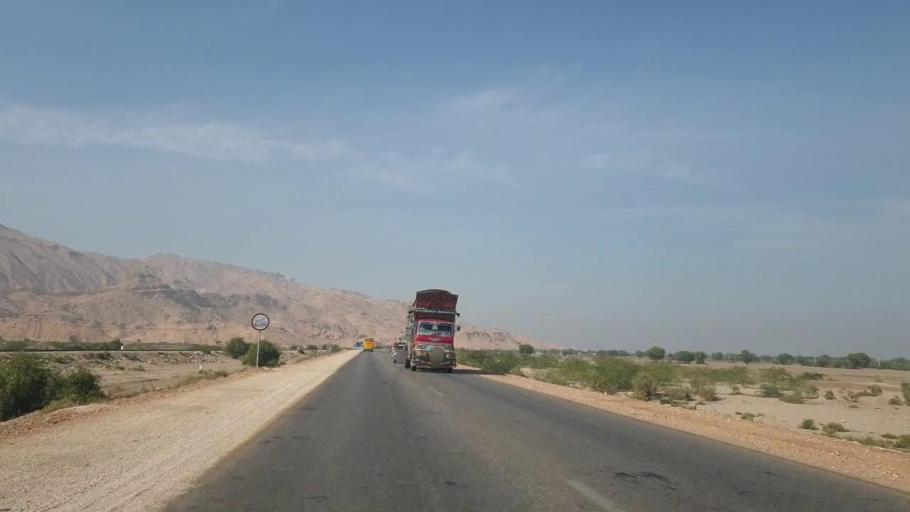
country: PK
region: Sindh
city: Sehwan
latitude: 26.2784
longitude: 67.8974
